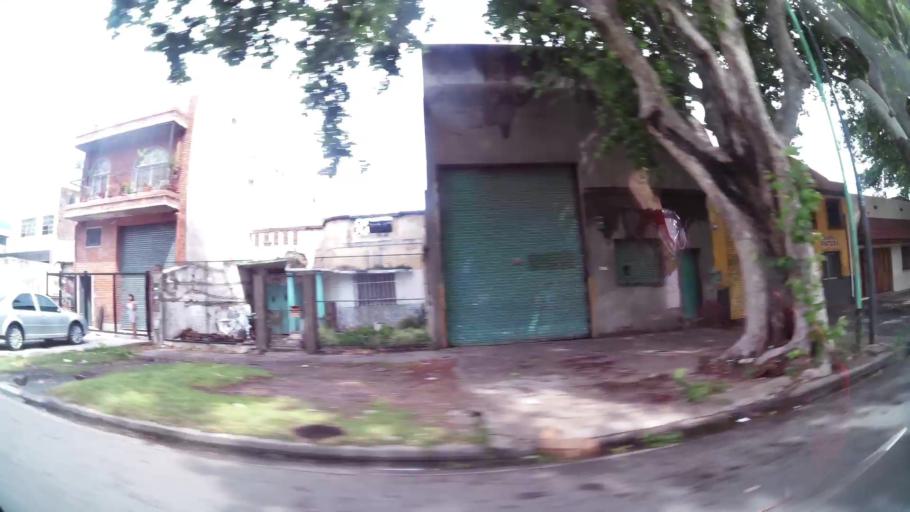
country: AR
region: Buenos Aires F.D.
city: Villa Lugano
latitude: -34.6618
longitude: -58.4313
